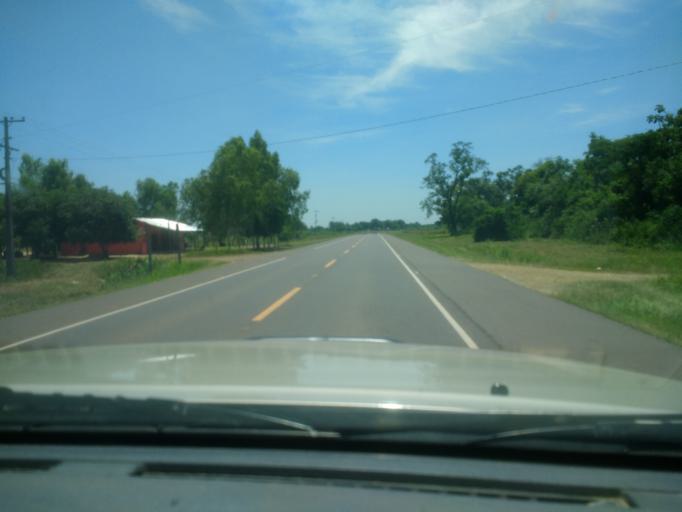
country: PY
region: San Pedro
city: Union
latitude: -24.7192
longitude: -56.5383
